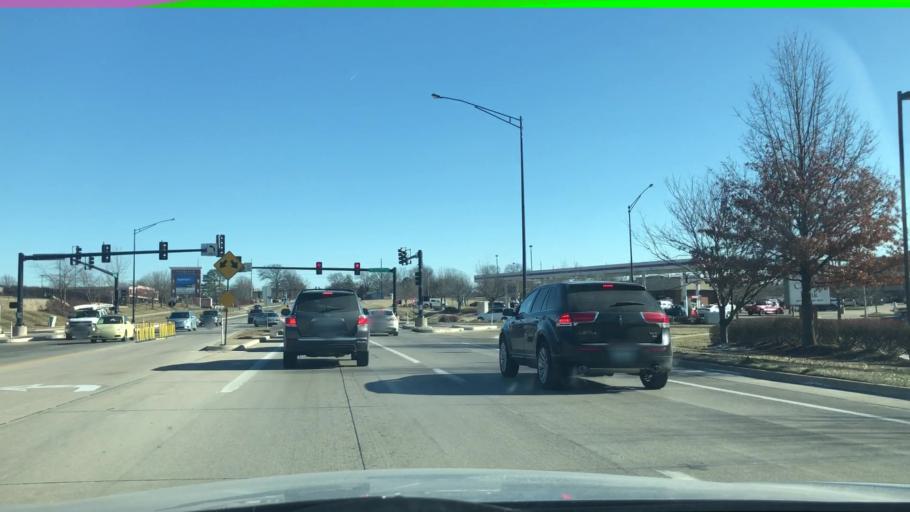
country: US
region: Missouri
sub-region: Boone County
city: Columbia
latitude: 38.9551
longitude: -92.3855
